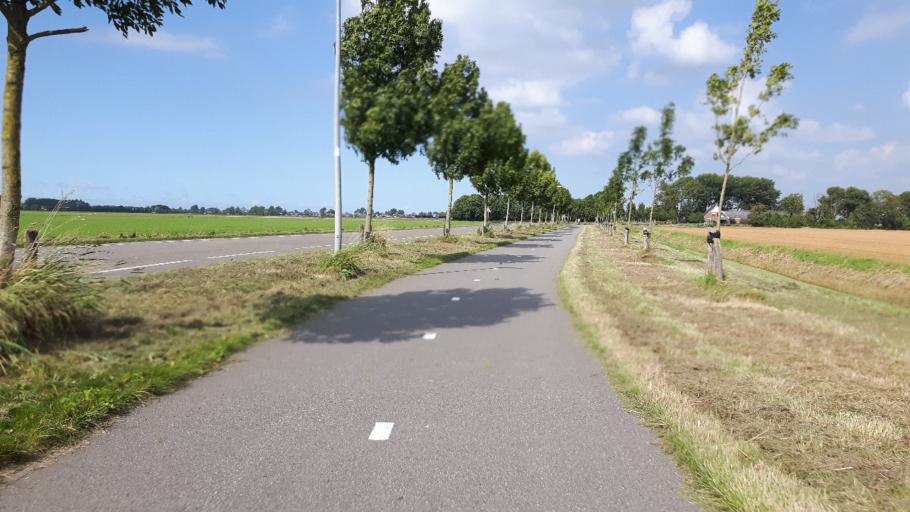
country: NL
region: North Holland
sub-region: Gemeente Medemblik
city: Opperdoes
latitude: 52.7116
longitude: 5.0918
